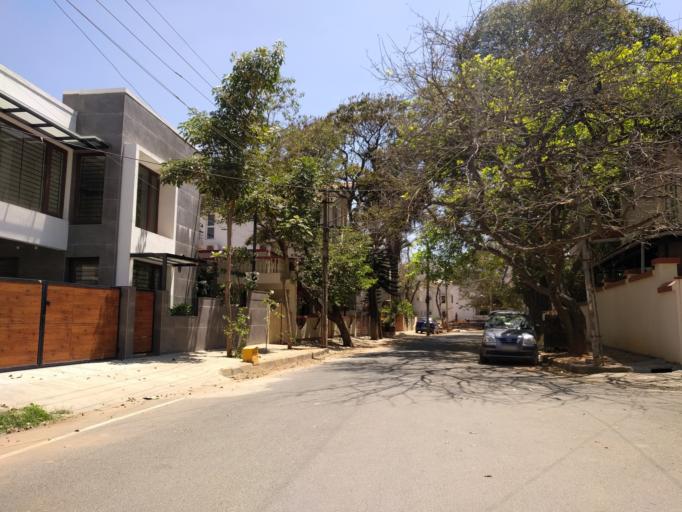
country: IN
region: Karnataka
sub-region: Bangalore Urban
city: Bangalore
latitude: 12.9274
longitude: 77.6363
